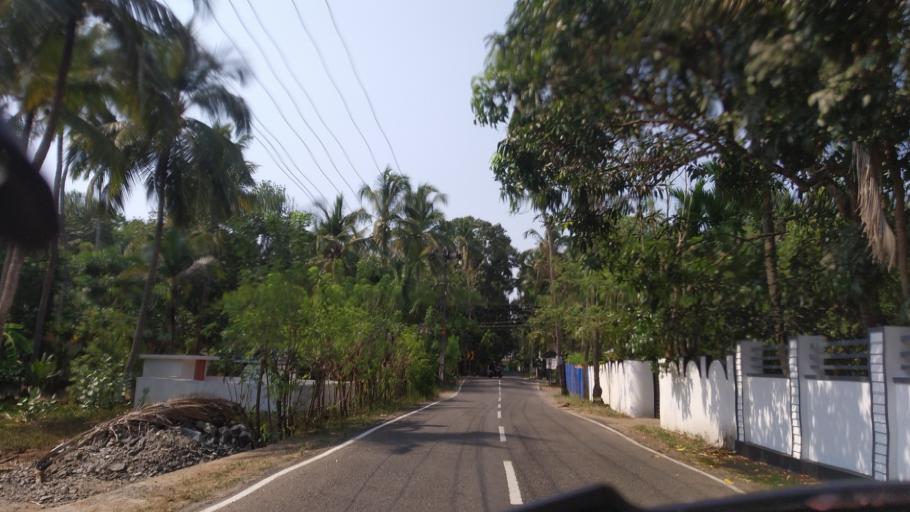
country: IN
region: Kerala
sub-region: Thrissur District
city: Thanniyam
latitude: 10.3978
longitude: 76.0943
